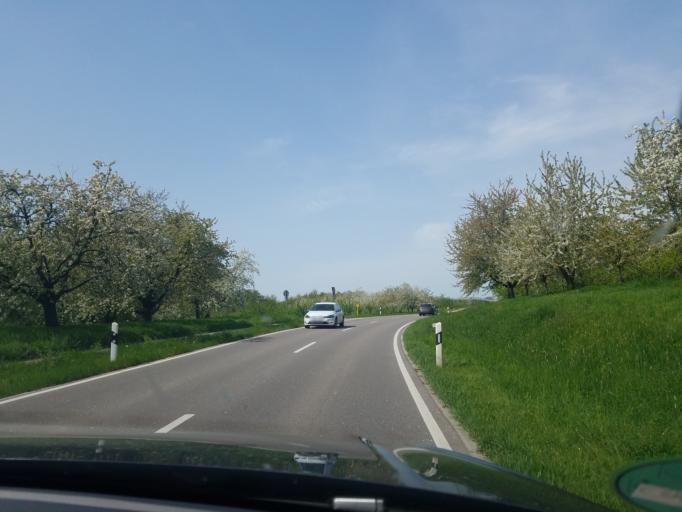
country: DE
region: Baden-Wuerttemberg
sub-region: Freiburg Region
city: Haslach
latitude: 48.5665
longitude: 8.0556
